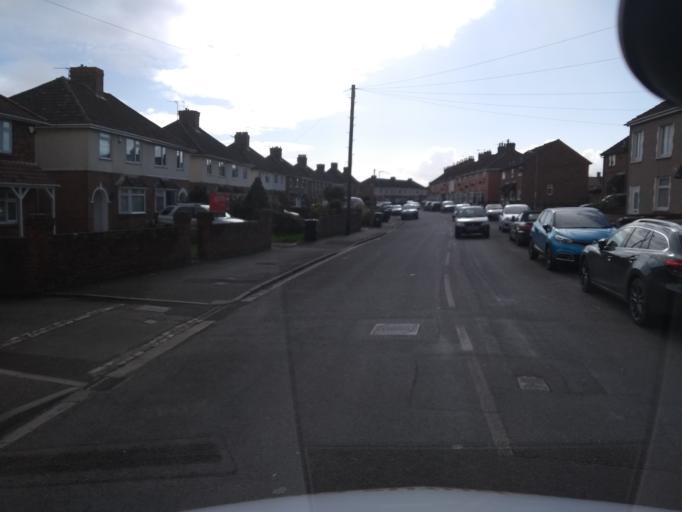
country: GB
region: England
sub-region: Somerset
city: Bridgwater
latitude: 51.1362
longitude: -3.0047
